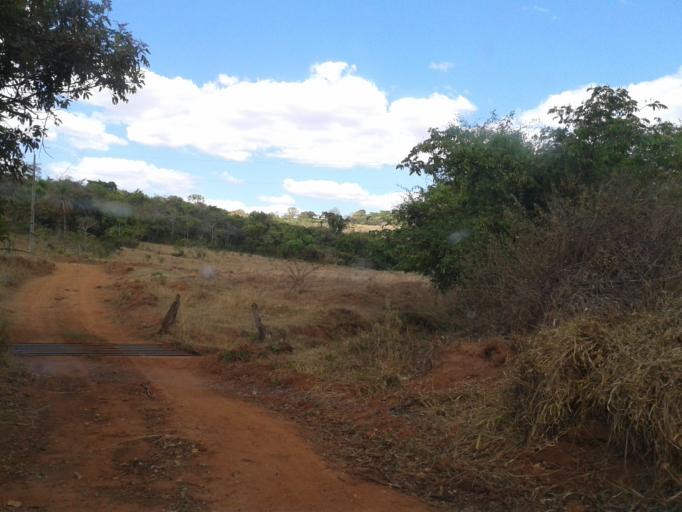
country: BR
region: Minas Gerais
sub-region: Monte Alegre De Minas
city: Monte Alegre de Minas
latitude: -18.7954
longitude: -49.0942
